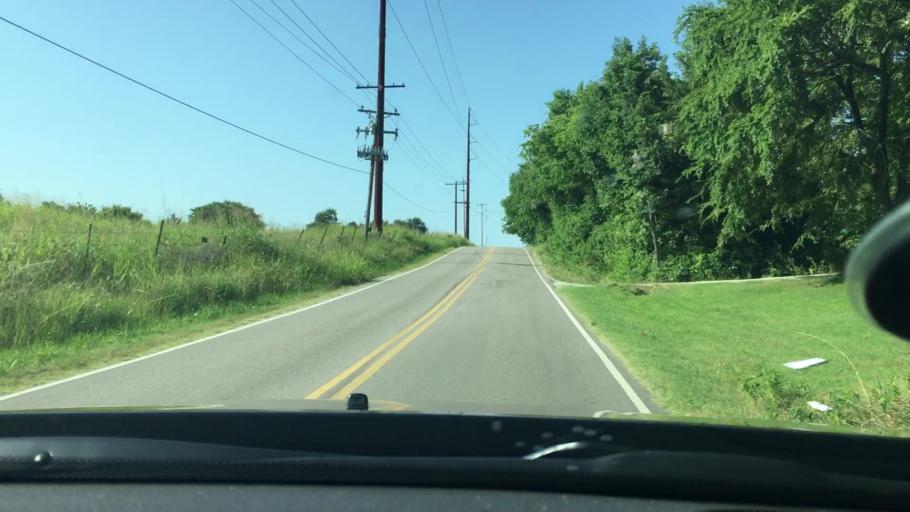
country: US
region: Oklahoma
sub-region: Pontotoc County
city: Ada
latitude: 34.7983
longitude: -96.6348
